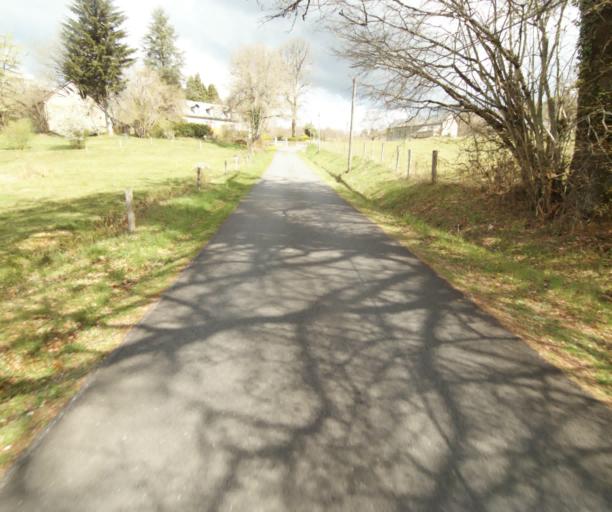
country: FR
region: Limousin
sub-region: Departement de la Correze
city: Correze
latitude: 45.2721
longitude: 1.8933
